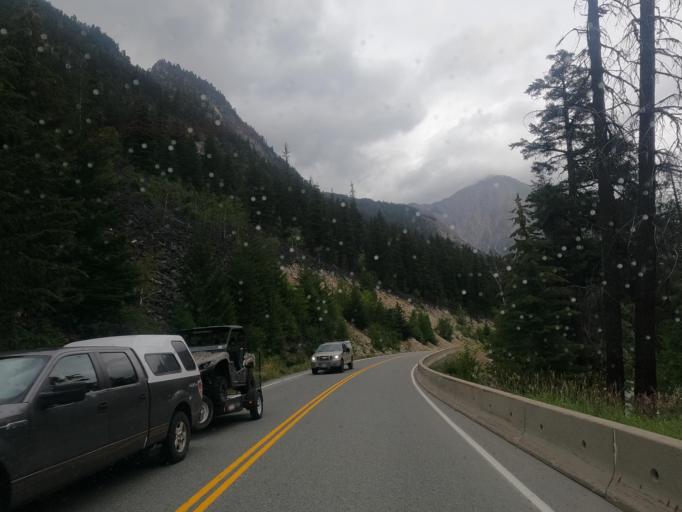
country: CA
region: British Columbia
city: Lillooet
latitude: 50.5149
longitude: -122.1709
